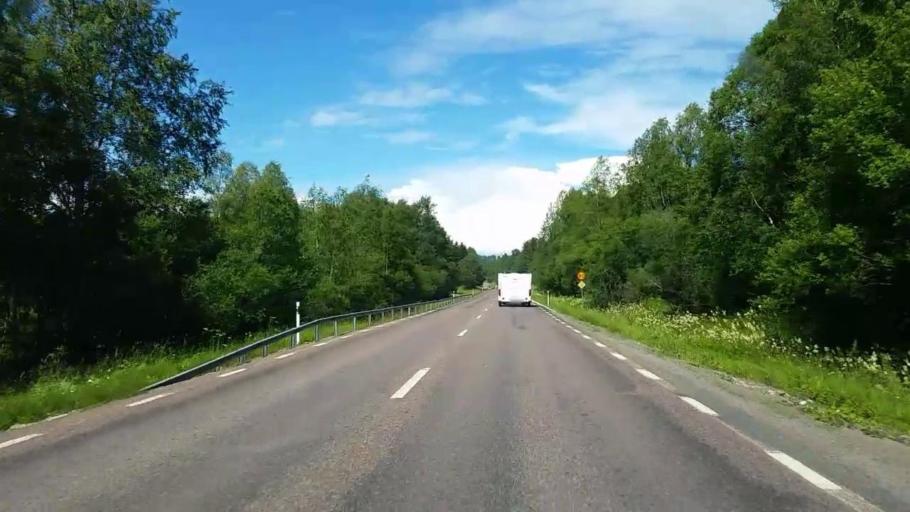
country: SE
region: Dalarna
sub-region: Rattviks Kommun
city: Raettvik
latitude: 60.9847
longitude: 15.2218
